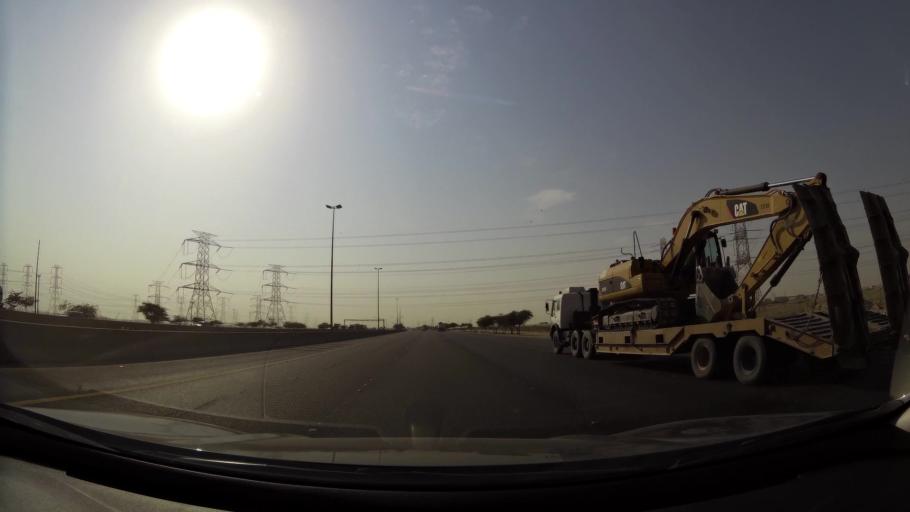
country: KW
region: Al Ahmadi
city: Al Ahmadi
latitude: 29.0051
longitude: 48.0952
